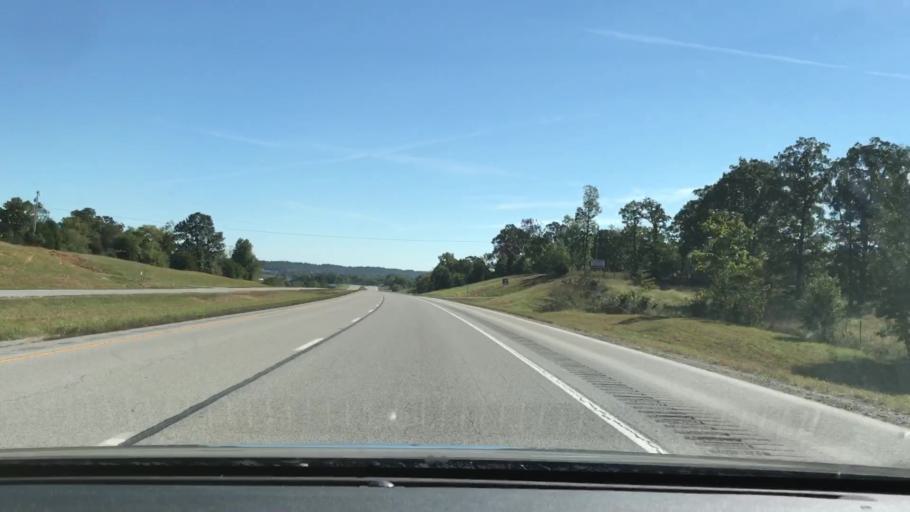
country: US
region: Kentucky
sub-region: Todd County
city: Elkton
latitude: 36.8207
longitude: -87.1888
